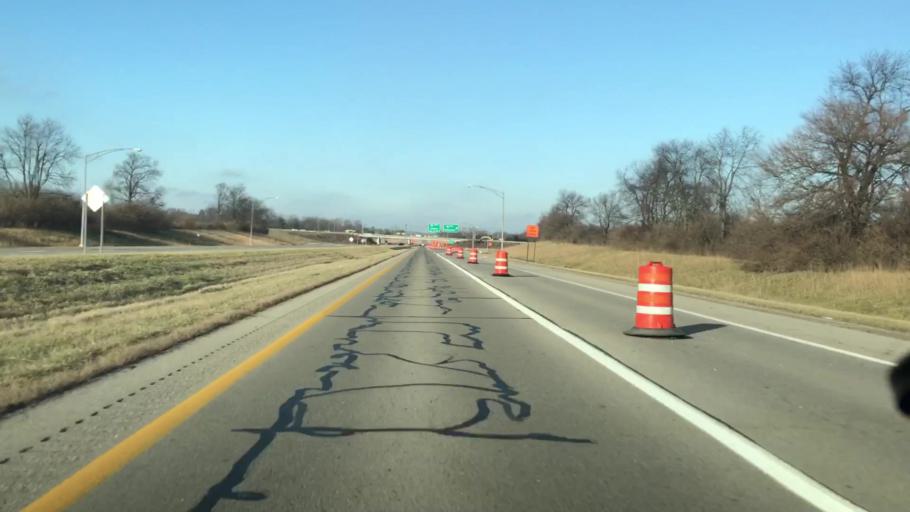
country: US
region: Ohio
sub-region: Clark County
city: Springfield
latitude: 39.8891
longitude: -83.8540
